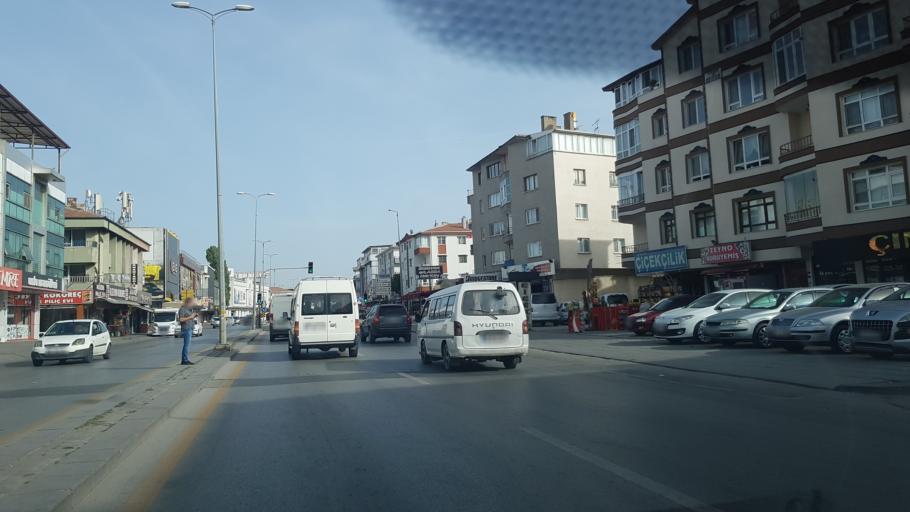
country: TR
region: Ankara
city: Etimesgut
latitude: 39.9546
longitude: 32.6325
